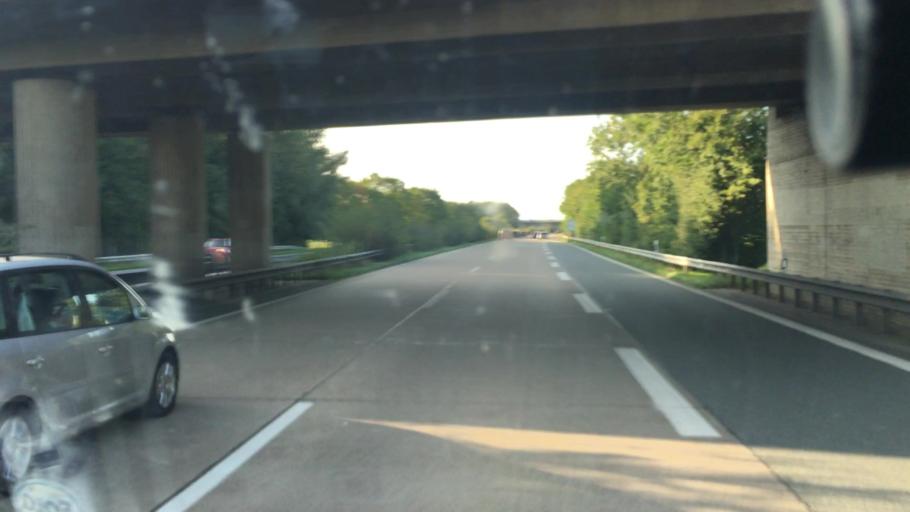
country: DE
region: Lower Saxony
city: Sande
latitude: 53.4871
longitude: 8.0043
